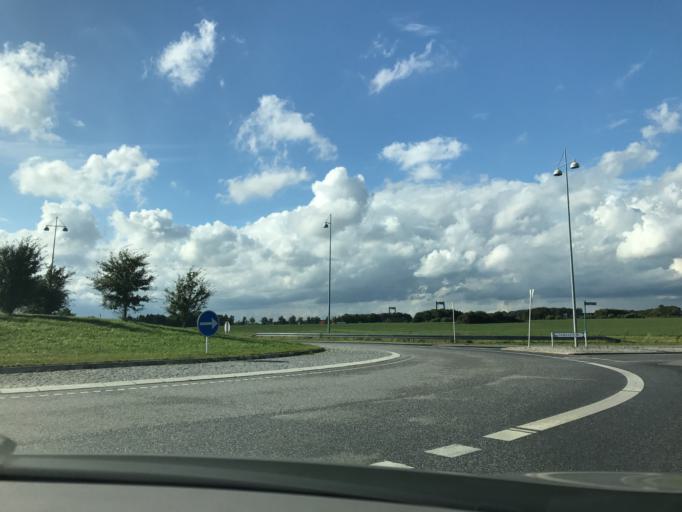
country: DK
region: South Denmark
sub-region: Middelfart Kommune
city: Strib
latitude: 55.5050
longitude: 9.7794
